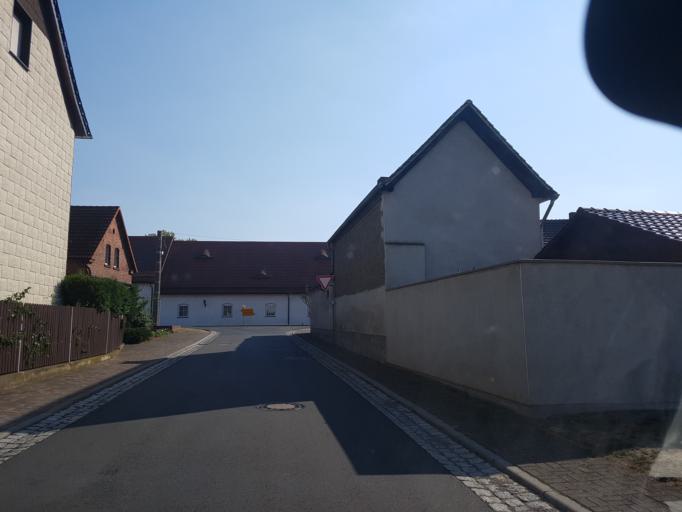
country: DE
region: Saxony-Anhalt
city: Prettin
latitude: 51.6467
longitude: 12.9826
